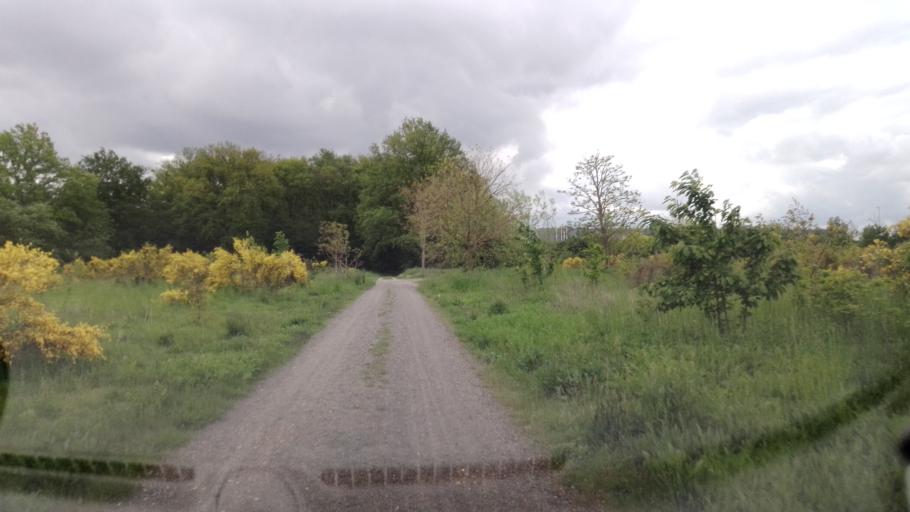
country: NL
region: Limburg
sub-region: Gemeente Venlo
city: Venlo
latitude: 51.4152
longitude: 6.1354
